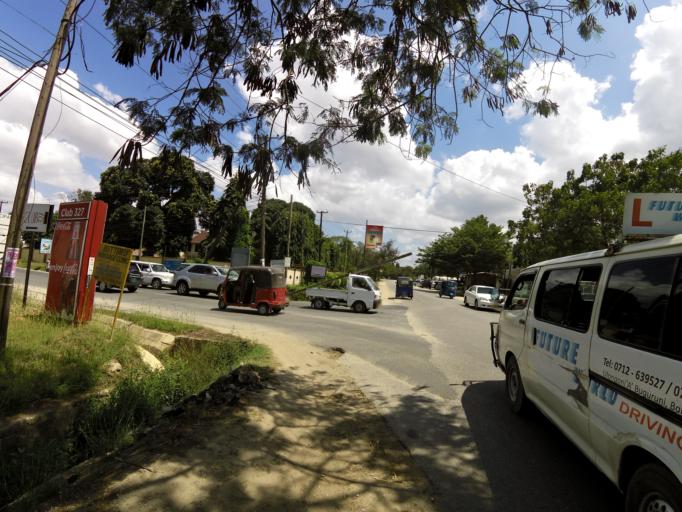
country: TZ
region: Dar es Salaam
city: Magomeni
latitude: -6.7653
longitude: 39.2485
